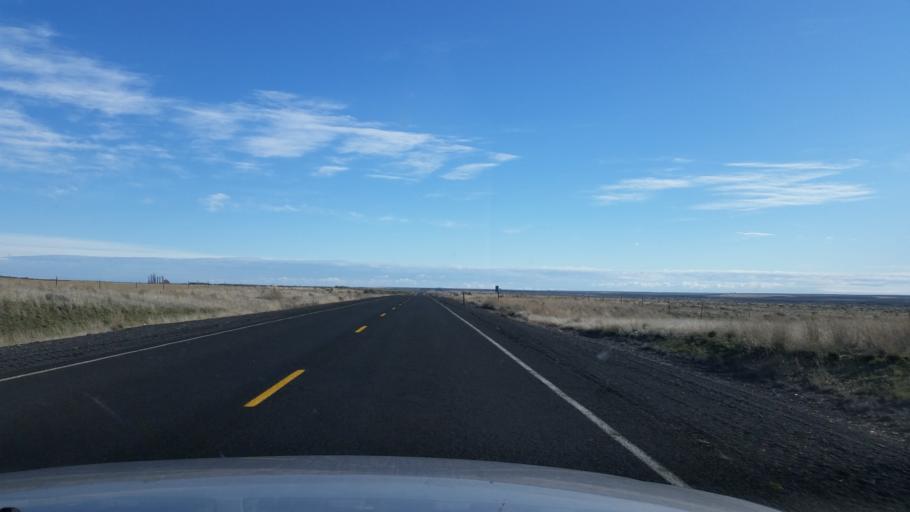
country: US
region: Washington
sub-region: Grant County
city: Warden
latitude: 47.3464
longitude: -118.9244
